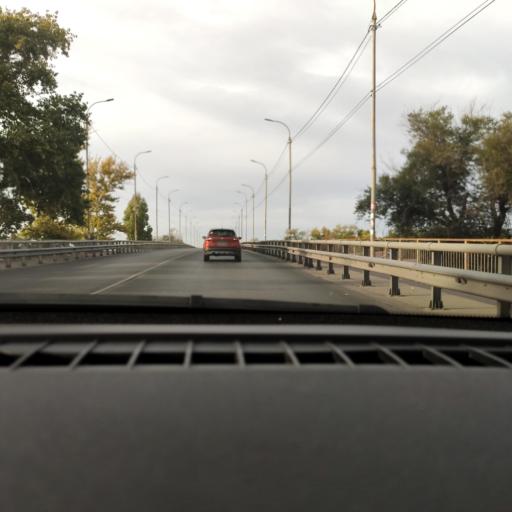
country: RU
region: Voronezj
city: Voronezh
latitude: 51.7257
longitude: 39.2616
